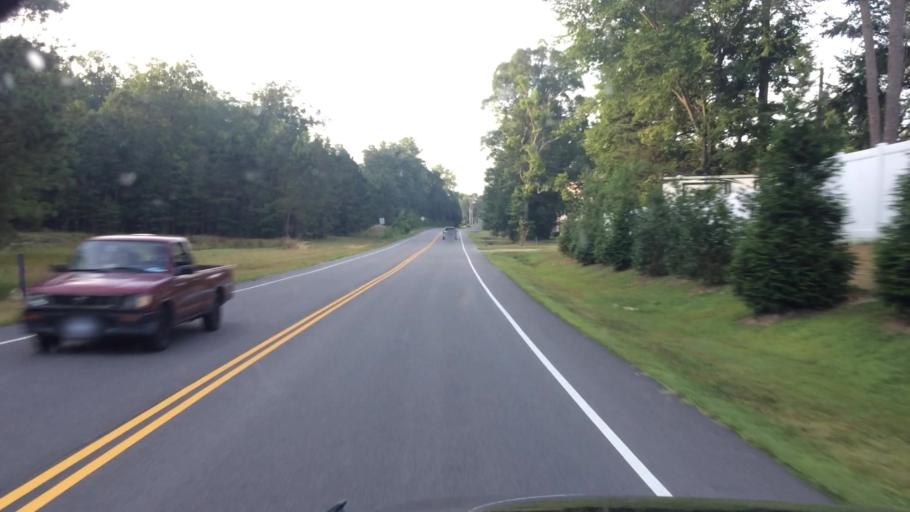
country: US
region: Virginia
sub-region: James City County
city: Williamsburg
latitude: 37.3063
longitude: -76.7280
